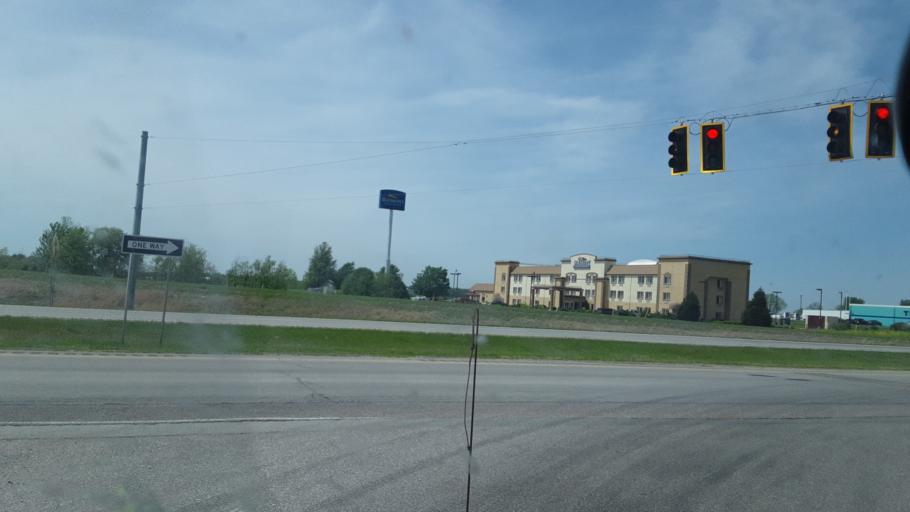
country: US
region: Indiana
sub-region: Gibson County
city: Haubstadt
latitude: 38.1691
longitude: -87.5502
